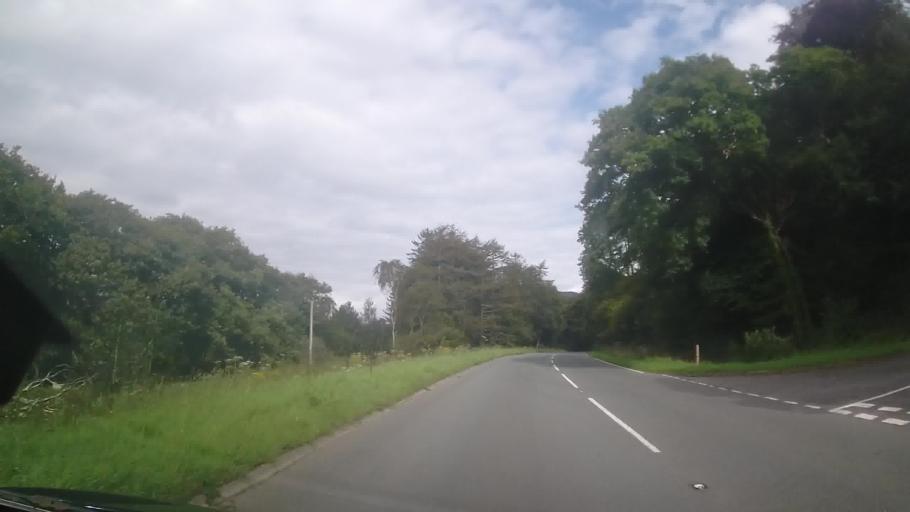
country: GB
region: Wales
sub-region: Gwynedd
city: Barmouth
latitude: 52.7336
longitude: -3.9725
